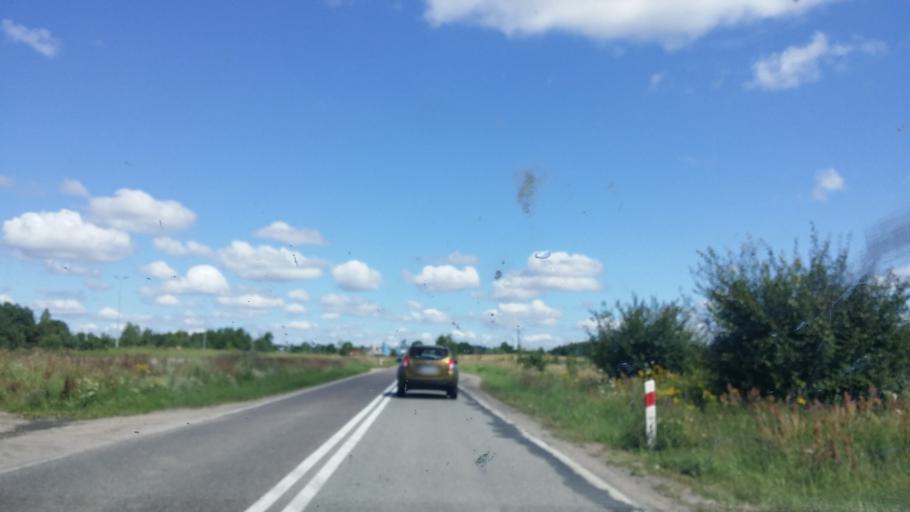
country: PL
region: West Pomeranian Voivodeship
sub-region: Powiat drawski
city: Drawsko Pomorskie
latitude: 53.5126
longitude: 15.7870
